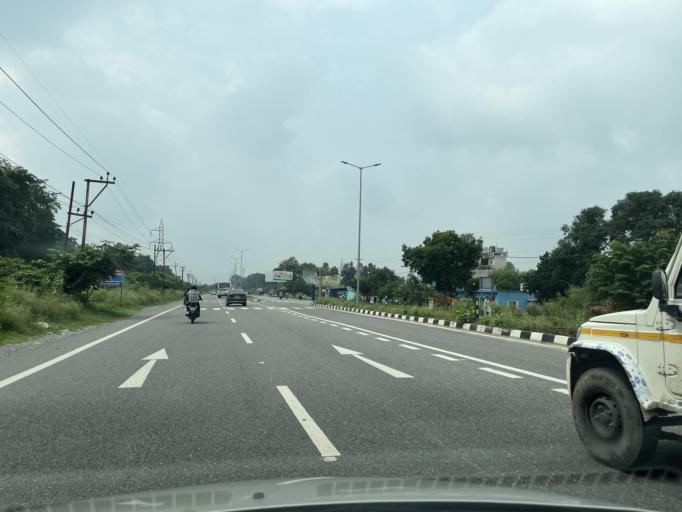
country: IN
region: Uttarakhand
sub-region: Dehradun
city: Doiwala
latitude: 30.1200
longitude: 78.1673
